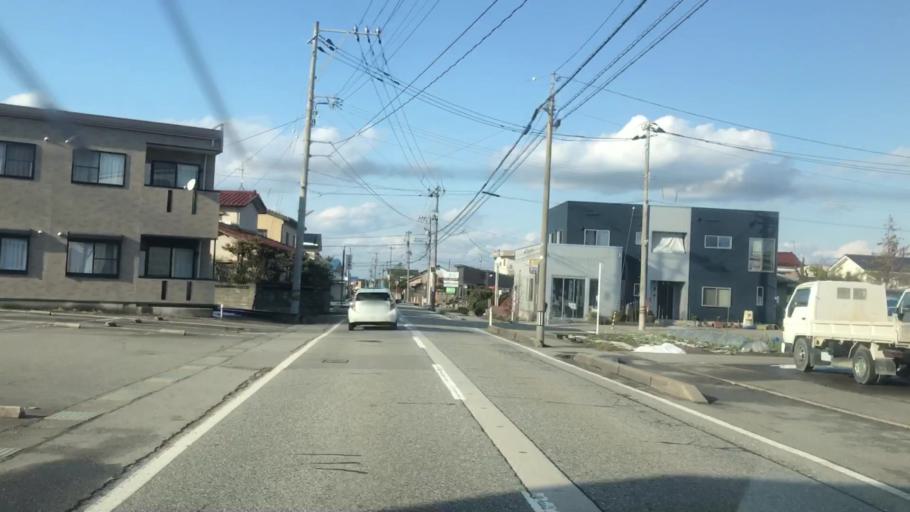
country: JP
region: Toyama
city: Toyama-shi
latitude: 36.6810
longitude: 137.2730
